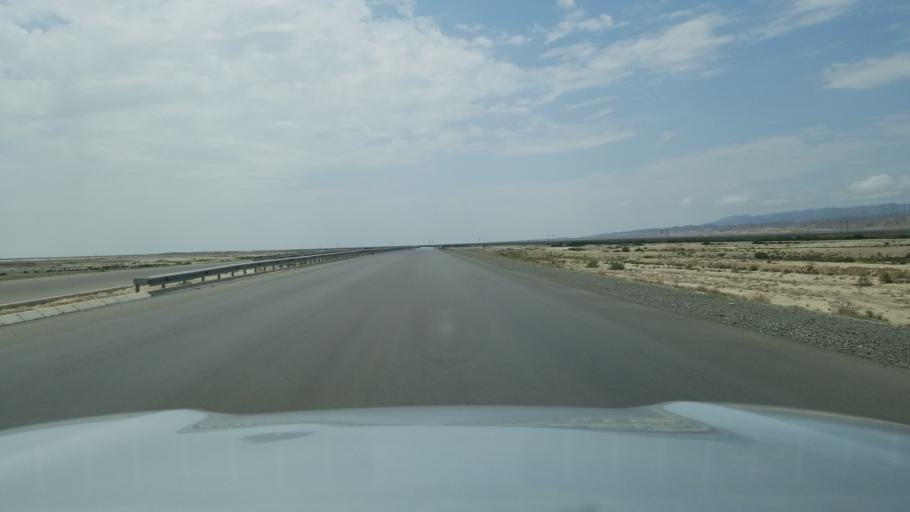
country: TM
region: Balkan
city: Gazanjyk
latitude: 39.2680
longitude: 55.1339
